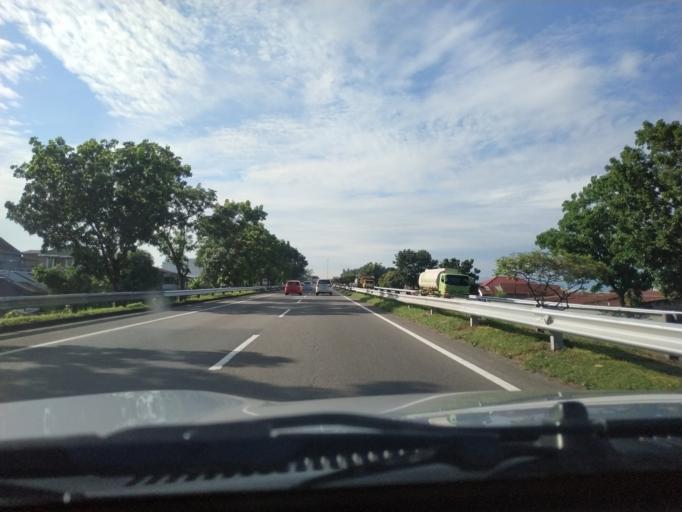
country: ID
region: North Sumatra
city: Medan
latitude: 3.5766
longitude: 98.7250
